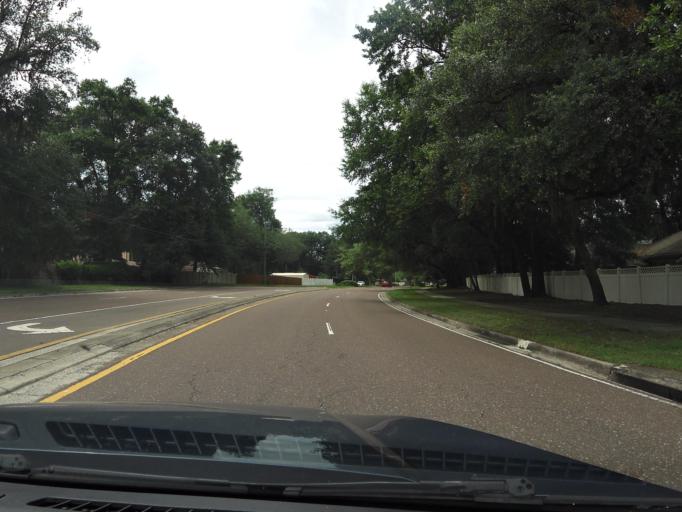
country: US
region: Florida
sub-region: Duval County
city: Jacksonville
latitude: 30.4321
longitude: -81.7161
